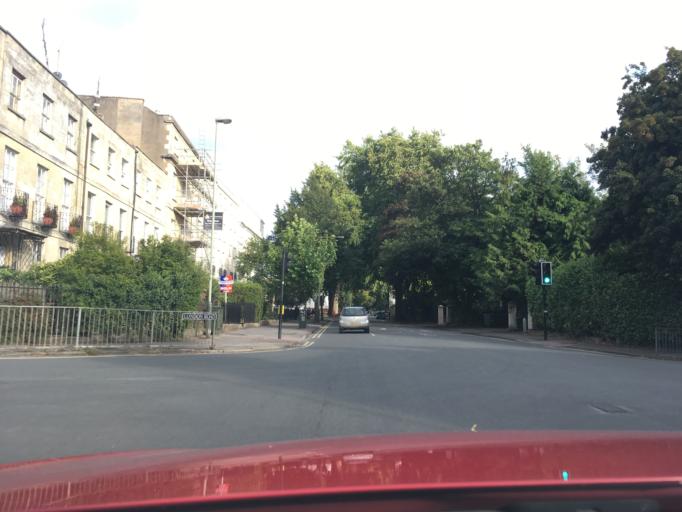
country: GB
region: England
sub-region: Gloucestershire
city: Cheltenham
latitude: 51.8967
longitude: -2.0692
